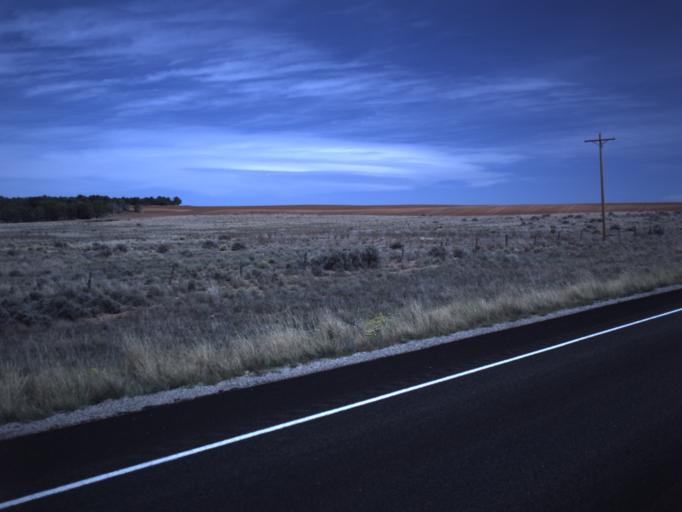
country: US
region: Utah
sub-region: San Juan County
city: Monticello
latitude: 37.8485
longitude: -109.1576
